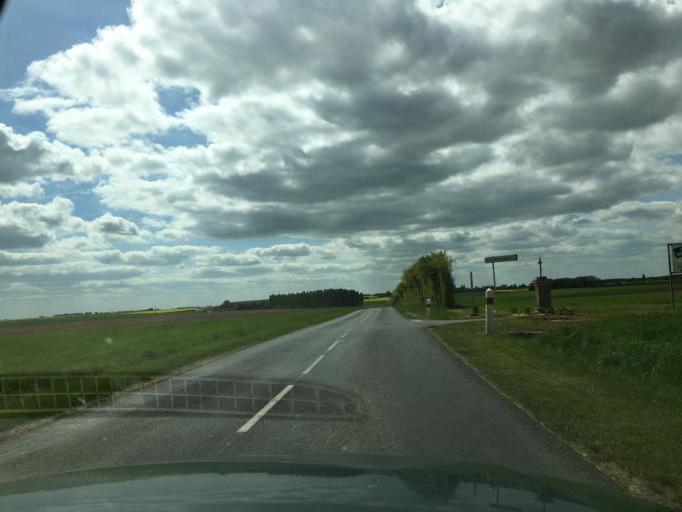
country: FR
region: Centre
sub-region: Departement du Loir-et-Cher
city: Oucques
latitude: 47.8116
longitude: 1.2693
